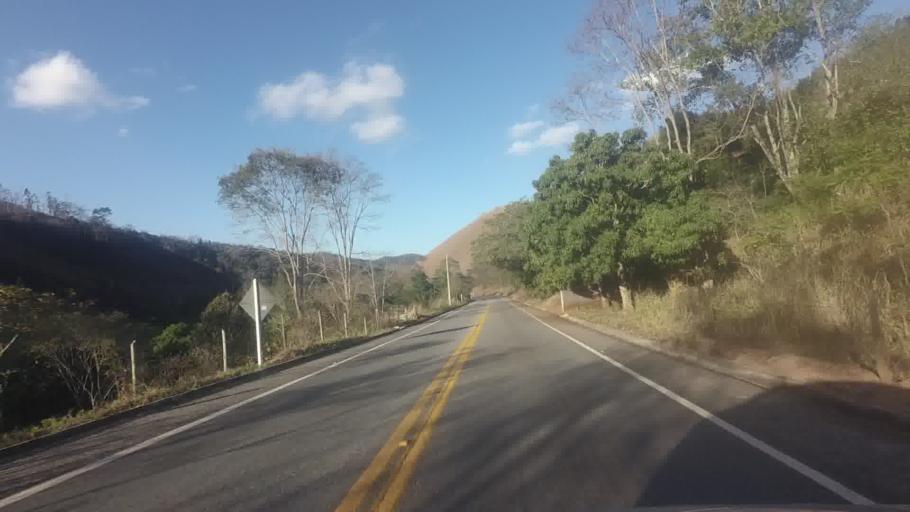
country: BR
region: Espirito Santo
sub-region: Cachoeiro De Itapemirim
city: Cachoeiro de Itapemirim
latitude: -20.8326
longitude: -41.2246
